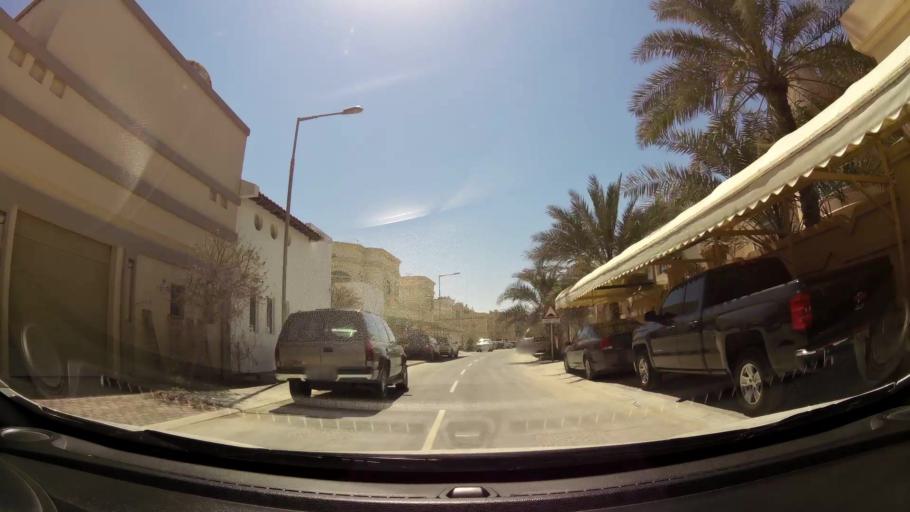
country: BH
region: Muharraq
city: Al Muharraq
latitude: 26.2818
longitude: 50.6022
